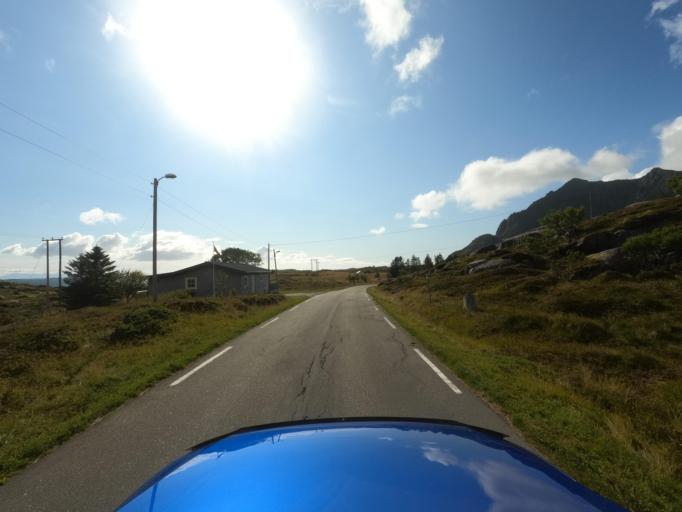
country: NO
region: Nordland
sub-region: Vestvagoy
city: Evjen
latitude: 68.2100
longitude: 14.0545
